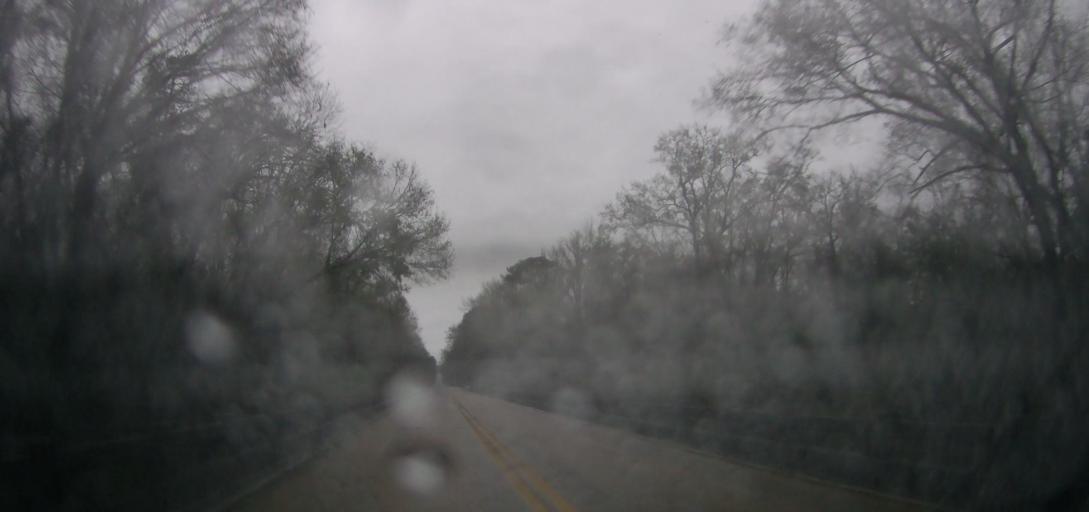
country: US
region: Alabama
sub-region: Autauga County
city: Pine Level
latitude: 32.5685
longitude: -86.6762
